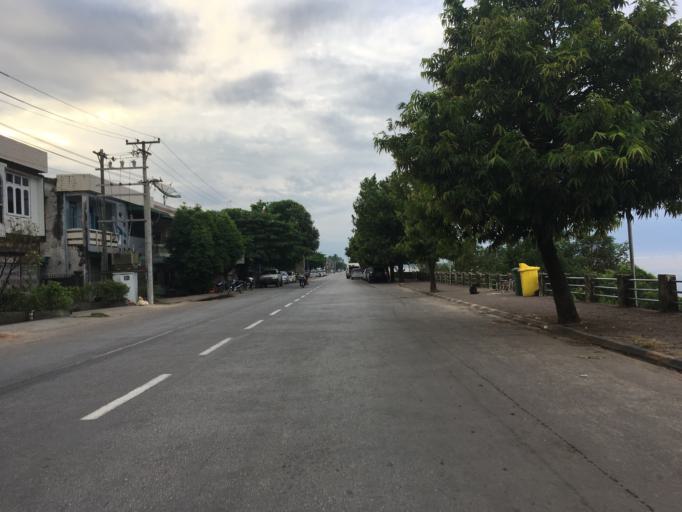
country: MM
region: Mon
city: Mawlamyine
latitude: 16.4803
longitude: 97.6189
